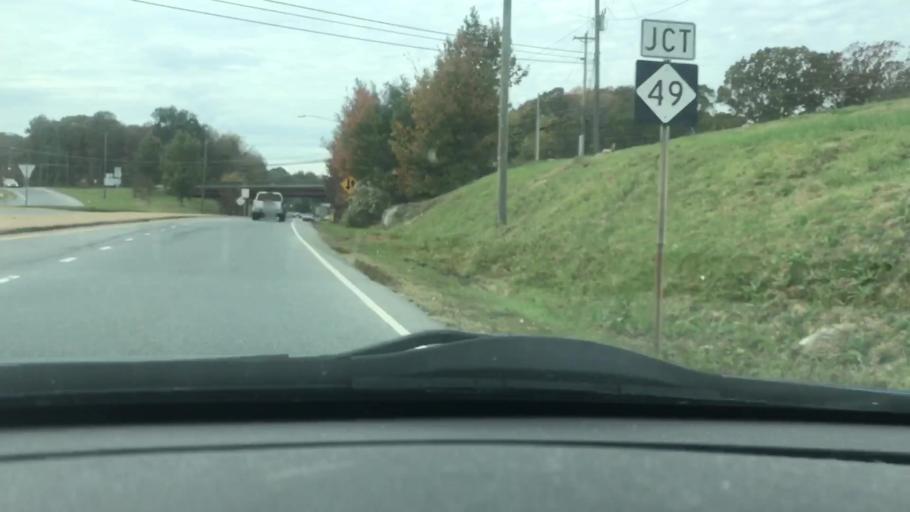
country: US
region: North Carolina
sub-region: Randolph County
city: Asheboro
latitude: 35.6855
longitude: -79.8344
